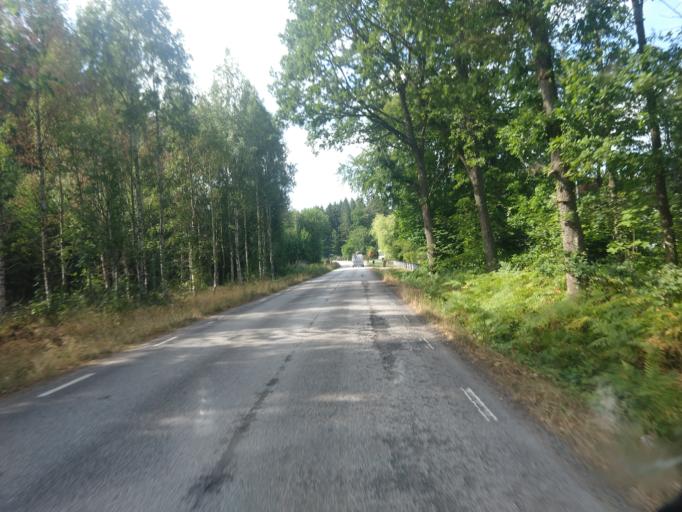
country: SE
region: Blekinge
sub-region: Karlskrona Kommun
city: Rodeby
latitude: 56.2406
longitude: 15.5639
